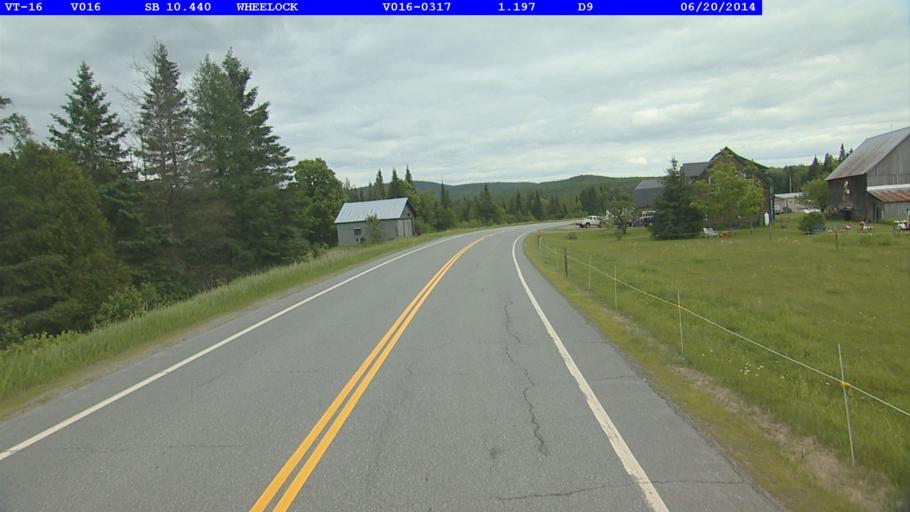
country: US
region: Vermont
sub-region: Caledonia County
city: Hardwick
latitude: 44.6137
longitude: -72.2084
